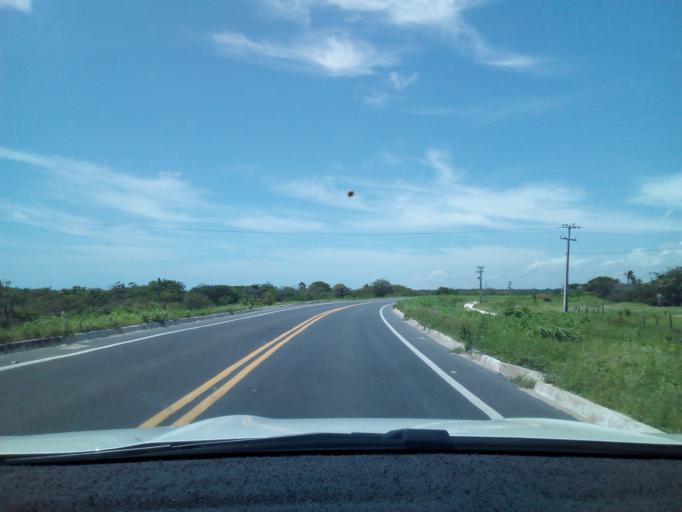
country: BR
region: Ceara
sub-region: Aracati
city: Aracati
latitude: -4.3966
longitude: -37.8525
